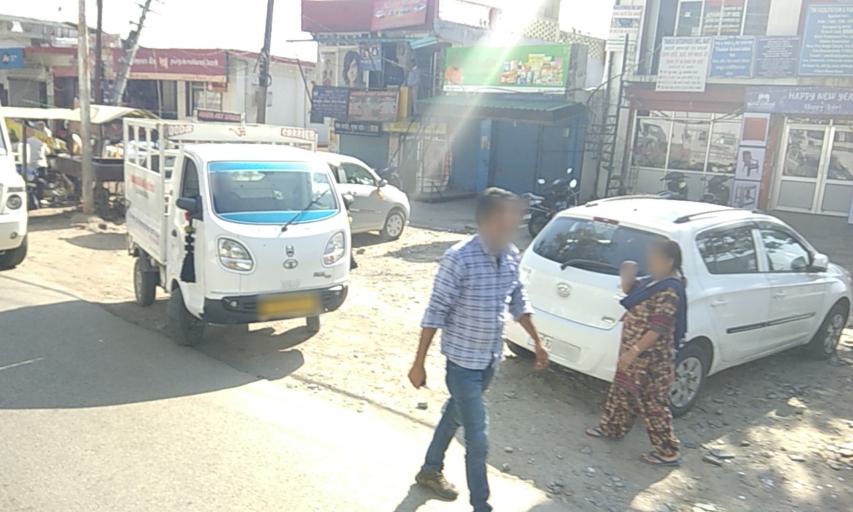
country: IN
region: Himachal Pradesh
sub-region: Kangra
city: Dharmsala
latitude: 32.1794
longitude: 76.3781
